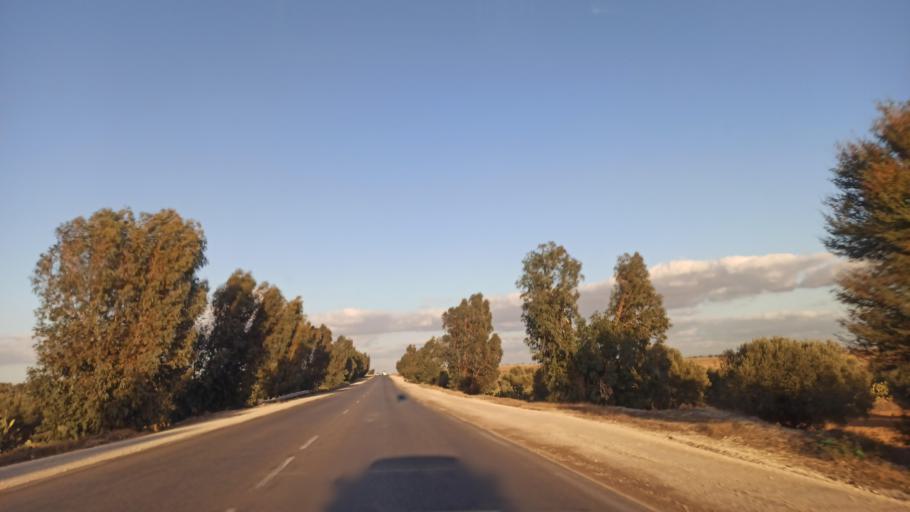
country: TN
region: Al Qayrawan
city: Sbikha
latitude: 35.8459
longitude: 10.1867
